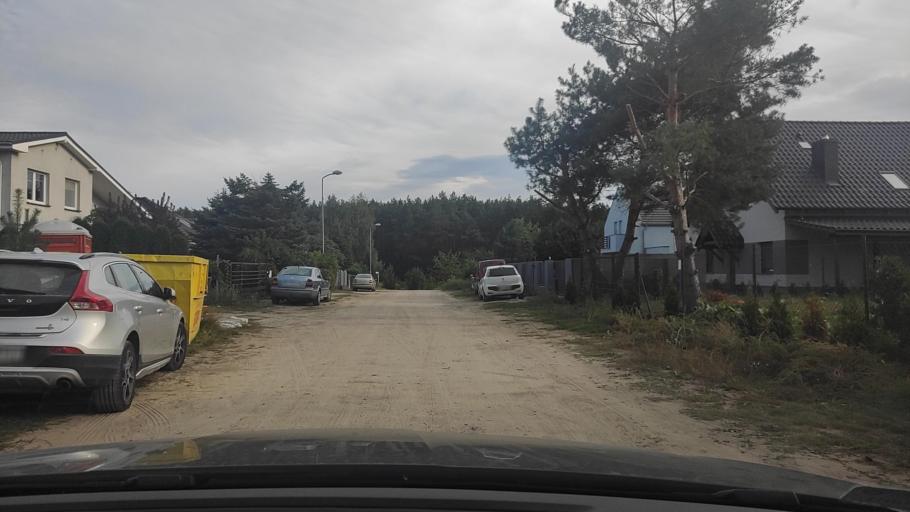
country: PL
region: Greater Poland Voivodeship
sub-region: Powiat poznanski
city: Kobylnica
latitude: 52.4323
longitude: 17.0325
